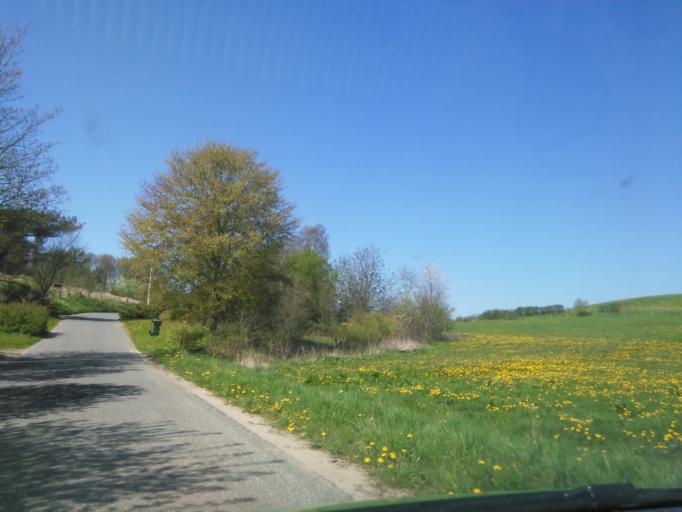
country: DK
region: Central Jutland
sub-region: Odder Kommune
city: Odder
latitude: 55.8987
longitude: 10.0524
